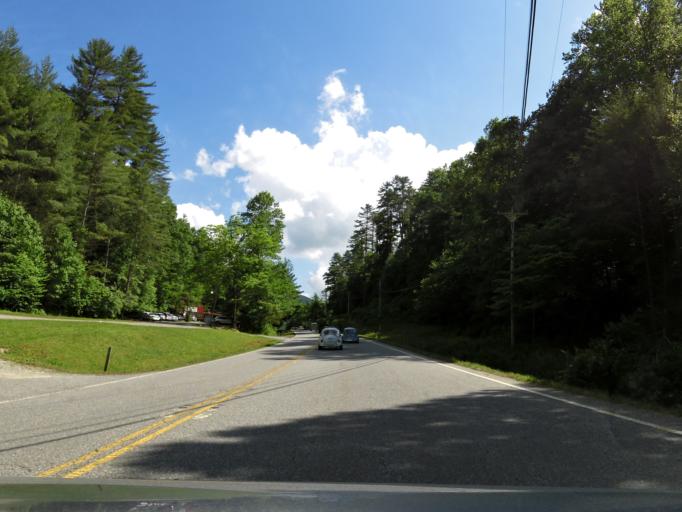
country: US
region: Georgia
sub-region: Towns County
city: Hiawassee
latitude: 34.8397
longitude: -83.7277
